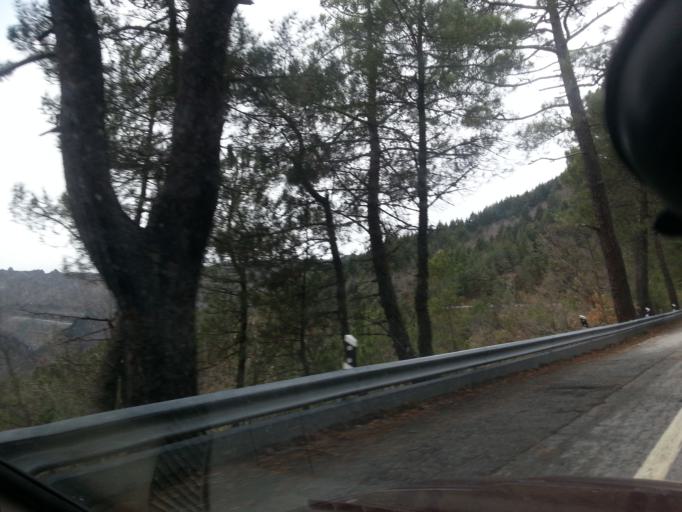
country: PT
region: Guarda
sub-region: Manteigas
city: Manteigas
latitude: 40.4156
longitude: -7.5351
